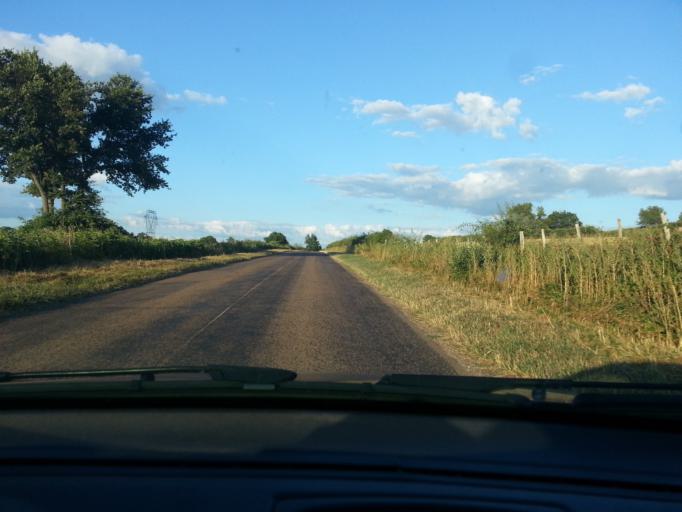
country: FR
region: Bourgogne
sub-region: Departement de Saone-et-Loire
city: Buxy
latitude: 46.7462
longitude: 4.6539
